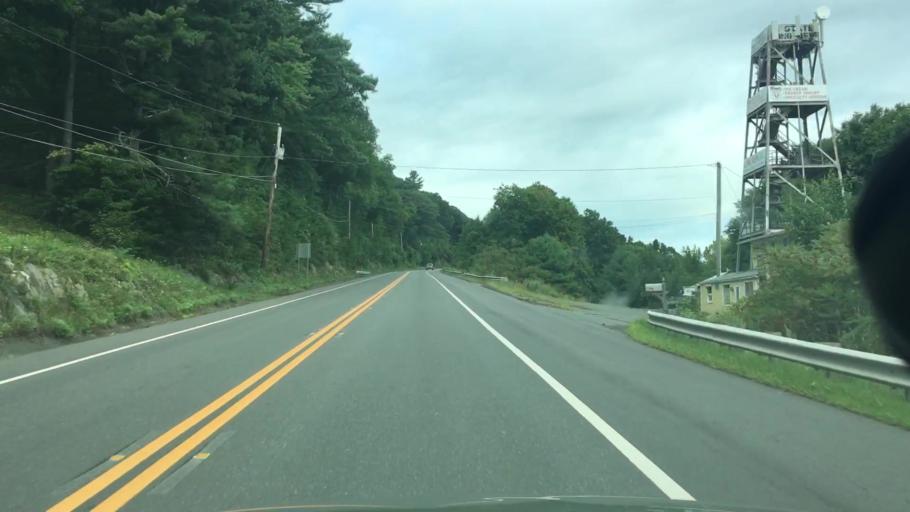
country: US
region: Massachusetts
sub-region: Franklin County
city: Greenfield
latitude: 42.5956
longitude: -72.6338
